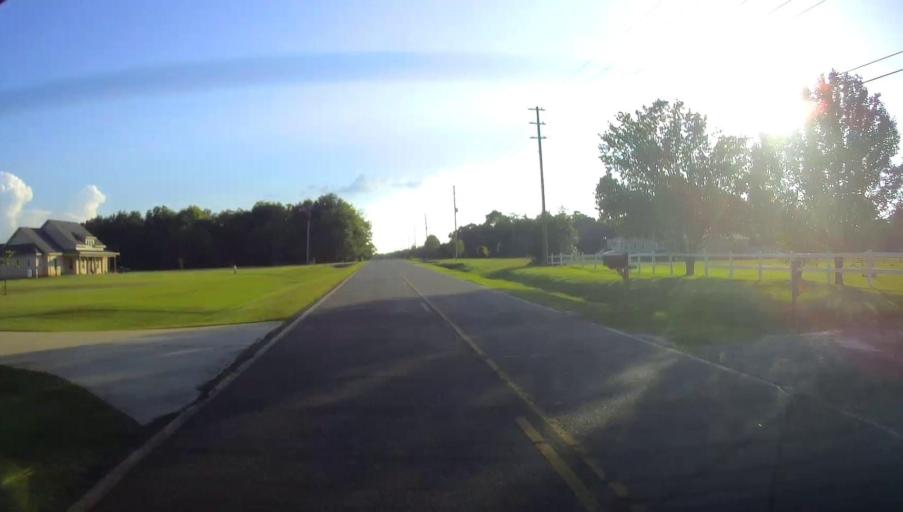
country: US
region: Georgia
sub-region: Peach County
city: Byron
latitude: 32.6359
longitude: -83.8029
